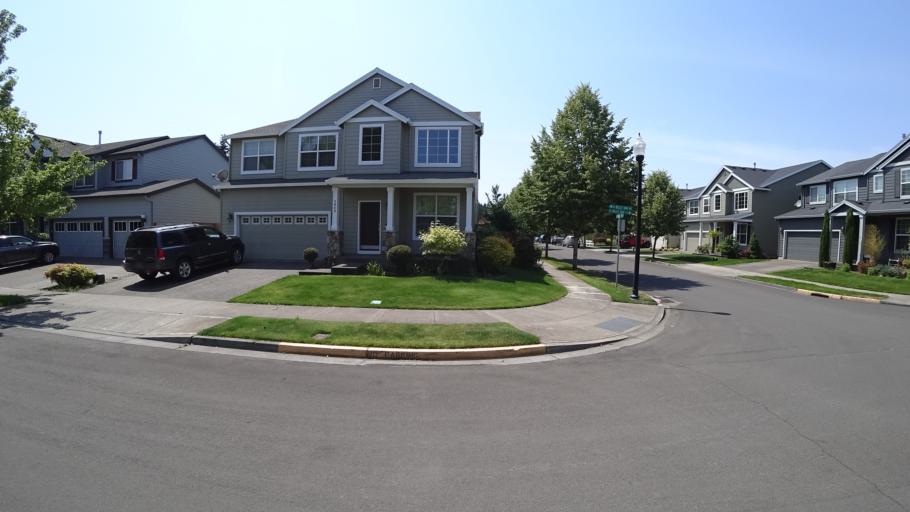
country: US
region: Oregon
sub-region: Washington County
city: Hillsboro
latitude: 45.4919
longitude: -122.9356
